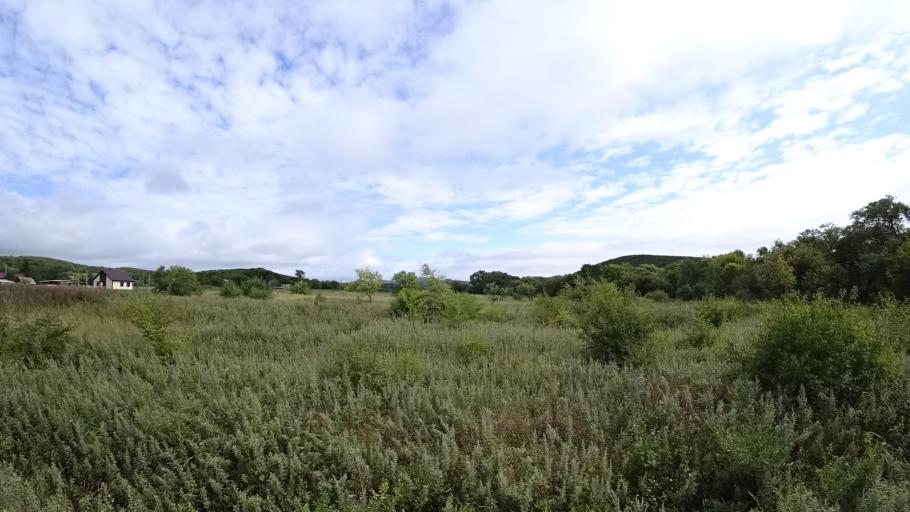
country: RU
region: Primorskiy
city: Lyalichi
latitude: 44.1392
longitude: 132.3750
